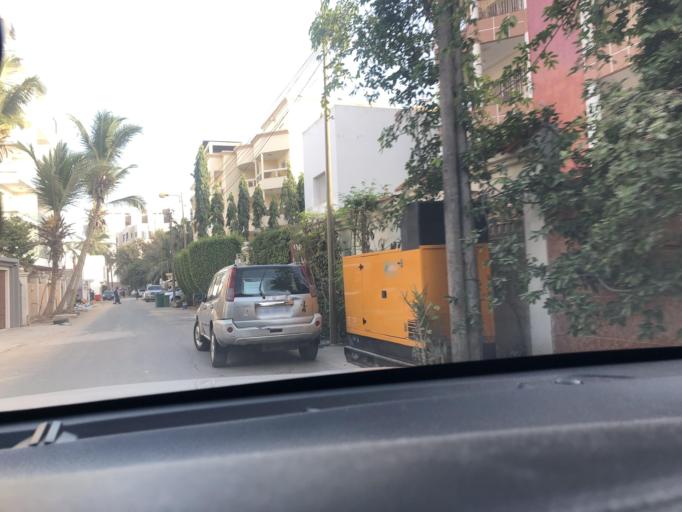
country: SN
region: Dakar
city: Mermoz Boabab
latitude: 14.7423
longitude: -17.5177
